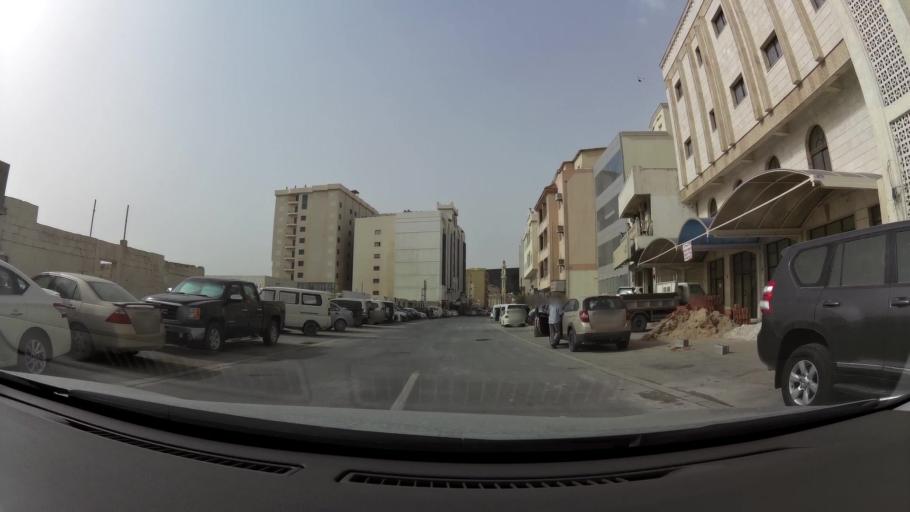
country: QA
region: Baladiyat ad Dawhah
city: Doha
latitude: 25.2764
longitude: 51.5474
